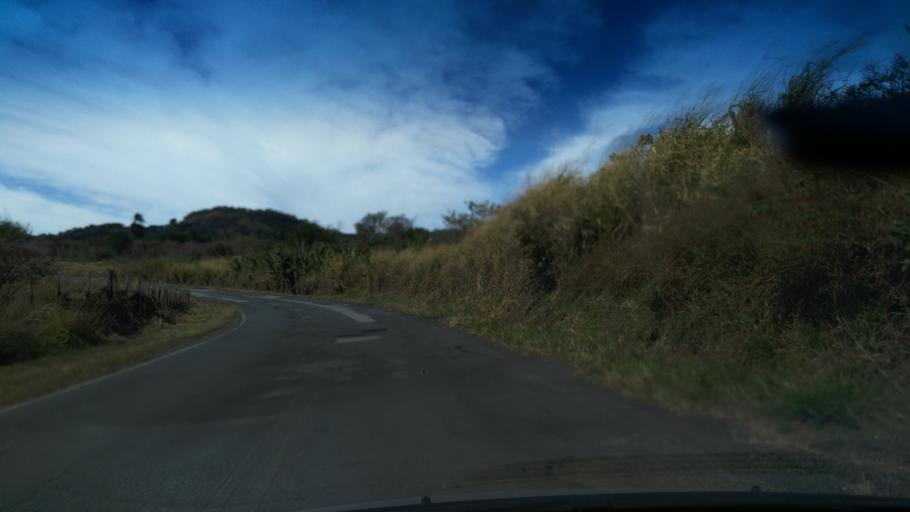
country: BR
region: Minas Gerais
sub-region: Andradas
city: Andradas
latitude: -22.0604
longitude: -46.3922
